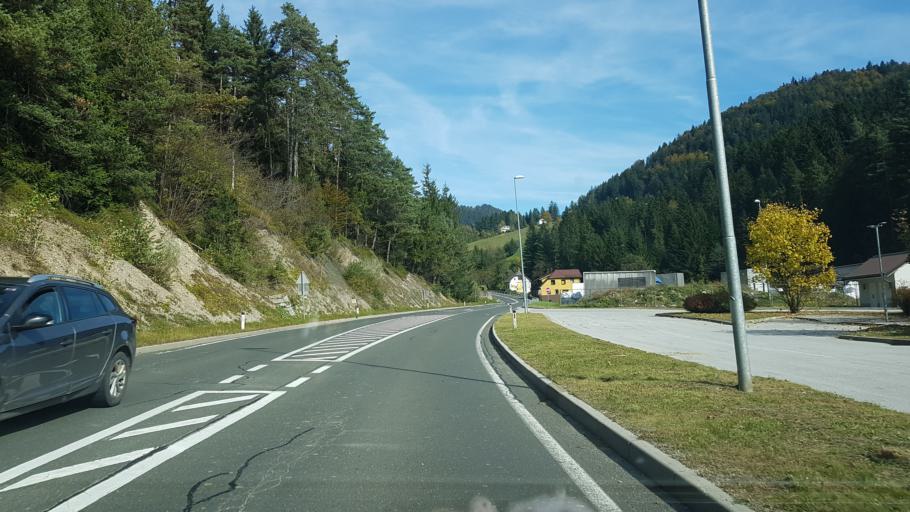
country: SI
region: Mislinja
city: Mislinja
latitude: 46.4362
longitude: 15.1908
